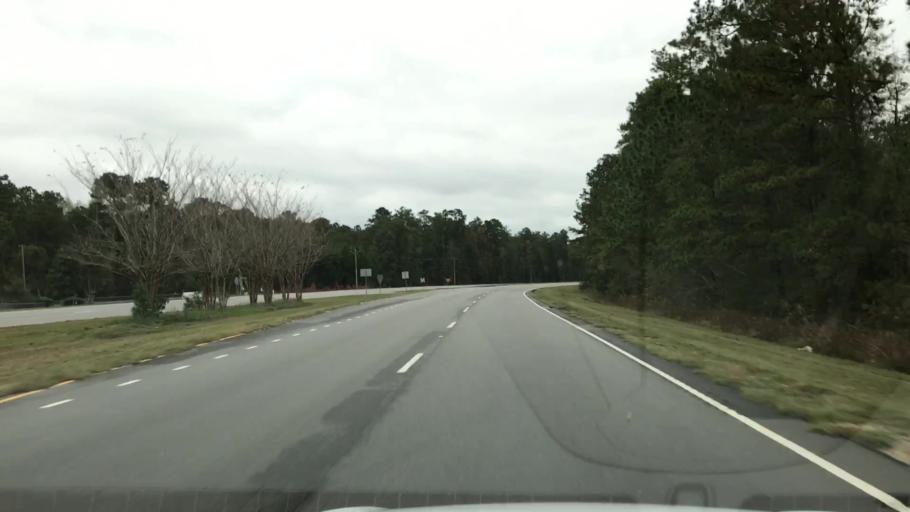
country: US
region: South Carolina
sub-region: Georgetown County
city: Georgetown
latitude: 33.2486
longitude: -79.3751
